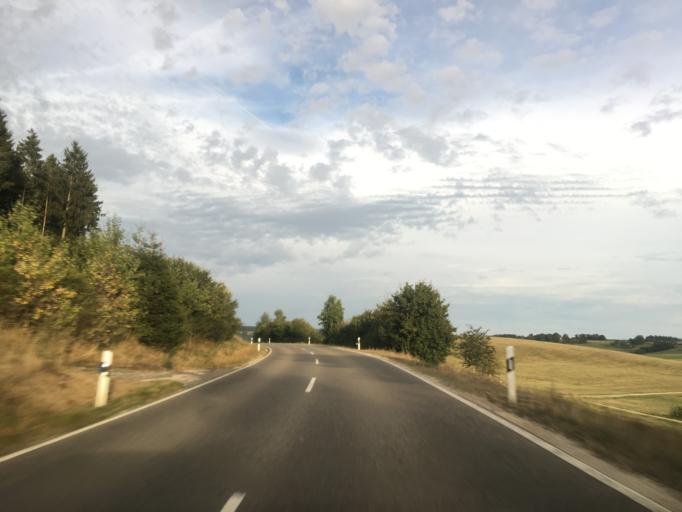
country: DE
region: Baden-Wuerttemberg
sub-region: Tuebingen Region
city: Sankt Johann
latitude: 48.4365
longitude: 9.3525
